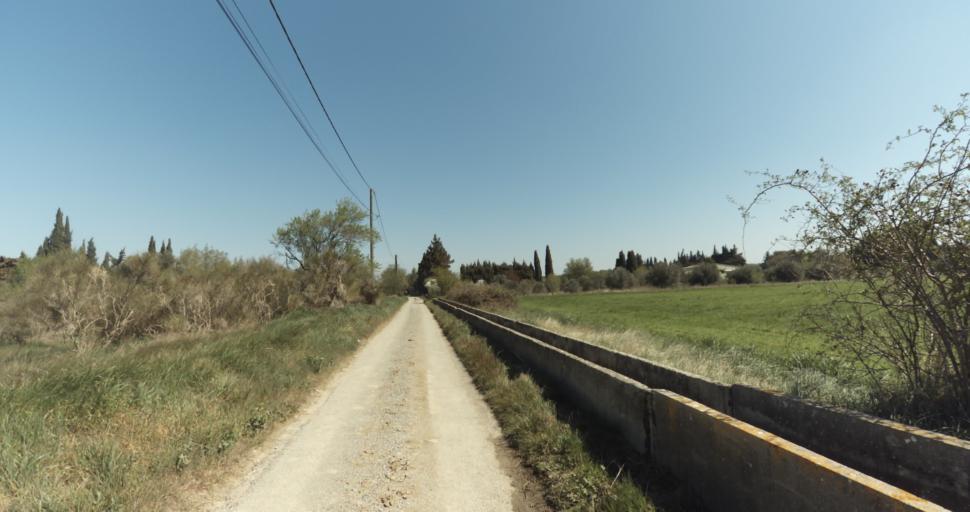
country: FR
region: Provence-Alpes-Cote d'Azur
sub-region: Departement des Bouches-du-Rhone
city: Pelissanne
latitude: 43.6172
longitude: 5.1474
